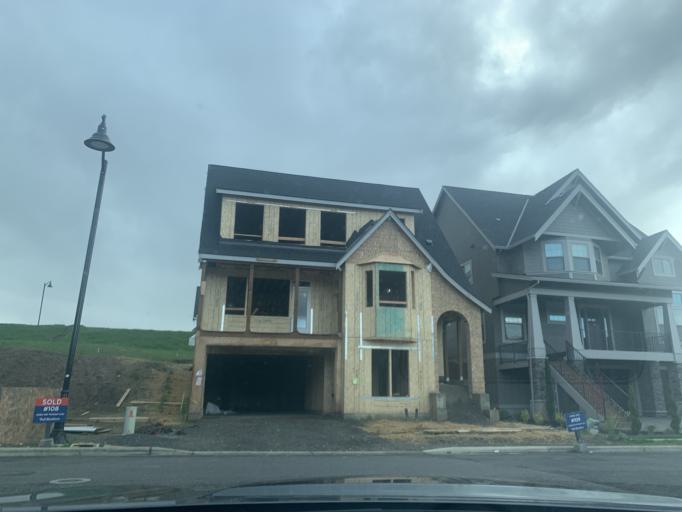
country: US
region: Oregon
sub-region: Washington County
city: Cedar Mill
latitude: 45.5513
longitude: -122.8032
